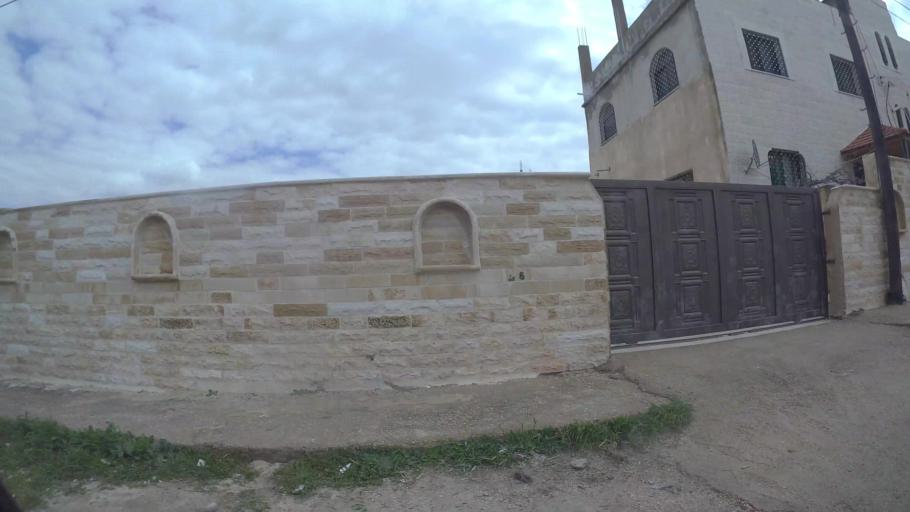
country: JO
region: Amman
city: Al Jubayhah
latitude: 32.0570
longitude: 35.8237
